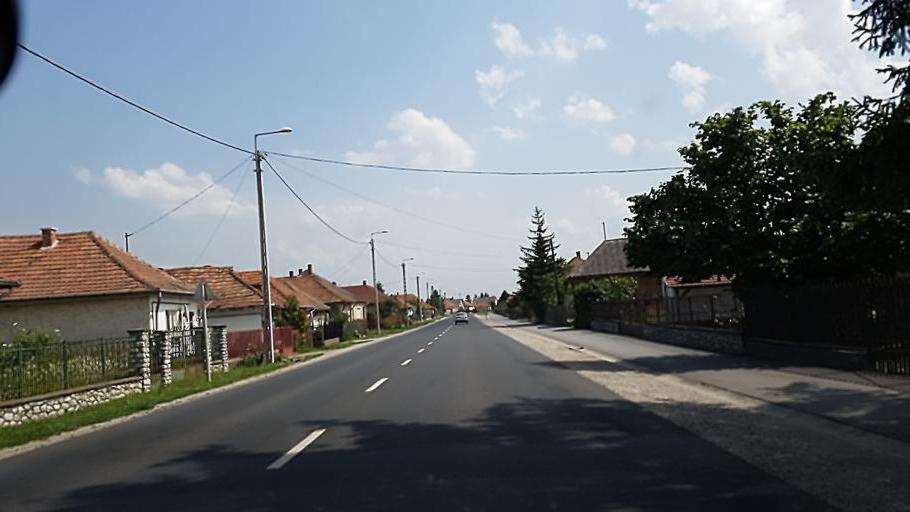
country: HU
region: Heves
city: Besenyotelek
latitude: 47.7188
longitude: 20.4201
